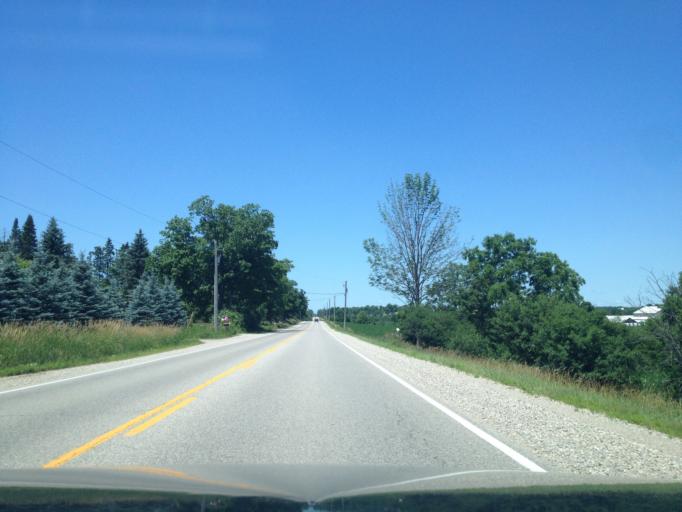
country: CA
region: Ontario
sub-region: Wellington County
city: Guelph
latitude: 43.6241
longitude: -80.2260
